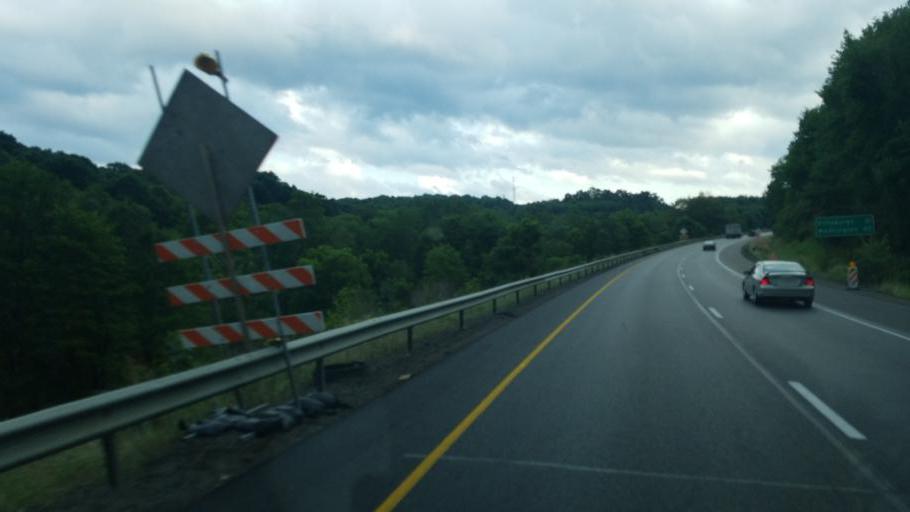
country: US
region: Pennsylvania
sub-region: Butler County
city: Evans City
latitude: 40.7492
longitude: -80.1075
